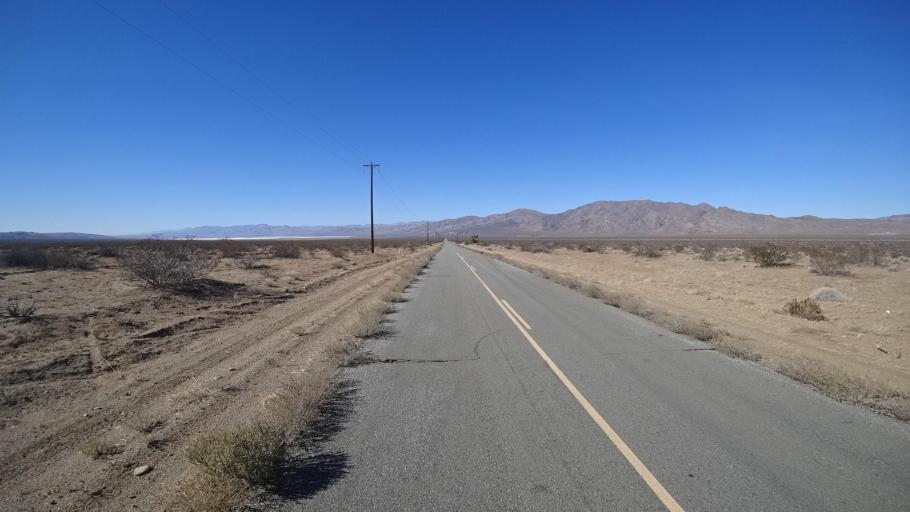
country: US
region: California
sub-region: Kern County
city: Ridgecrest
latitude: 35.3856
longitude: -117.7296
